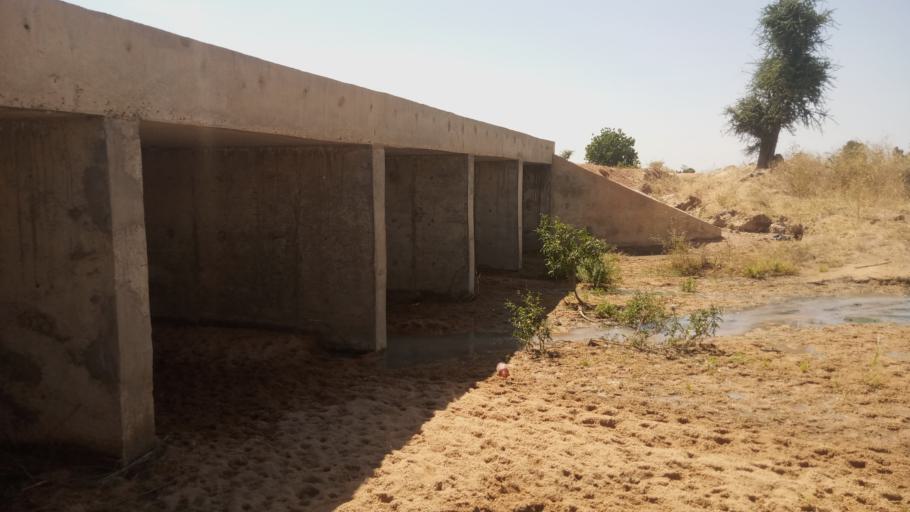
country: NG
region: Borno
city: Shani
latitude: 9.8632
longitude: 12.0910
